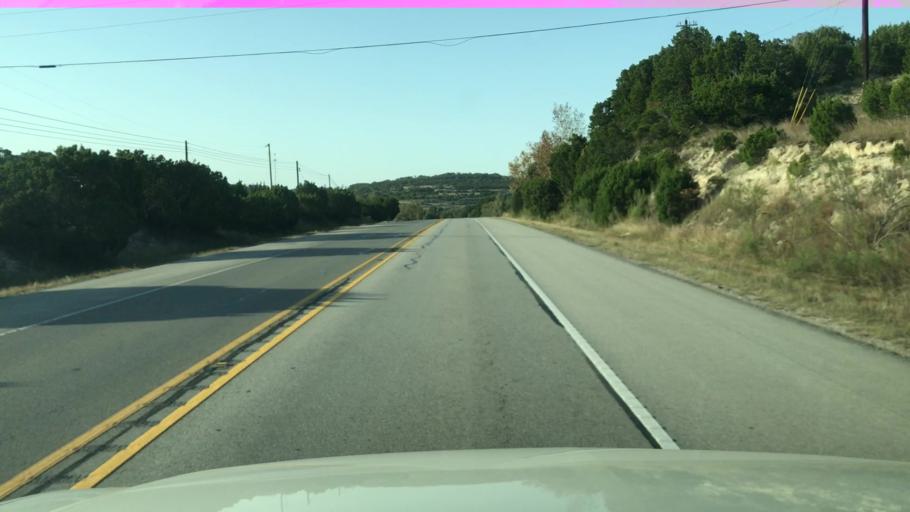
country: US
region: Texas
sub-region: Blanco County
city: Johnson City
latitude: 30.1907
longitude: -98.3774
